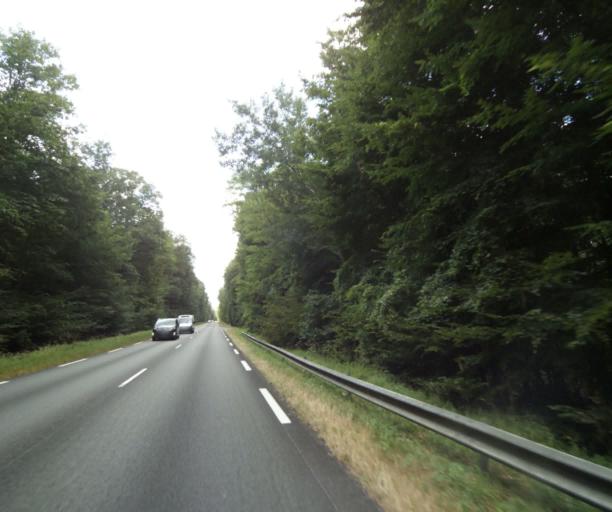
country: FR
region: Ile-de-France
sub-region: Departement de Seine-et-Marne
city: Thomery
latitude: 48.4209
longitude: 2.7850
